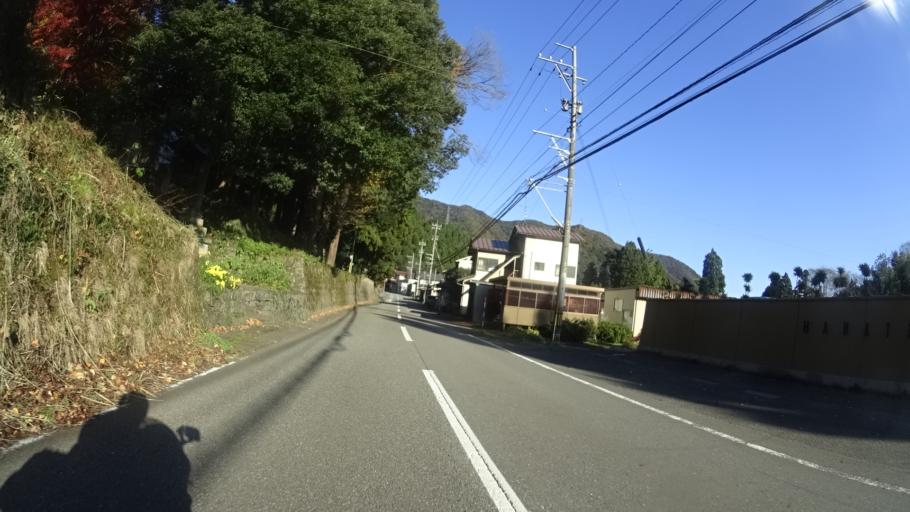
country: JP
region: Fukui
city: Maruoka
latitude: 36.2269
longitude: 136.3603
